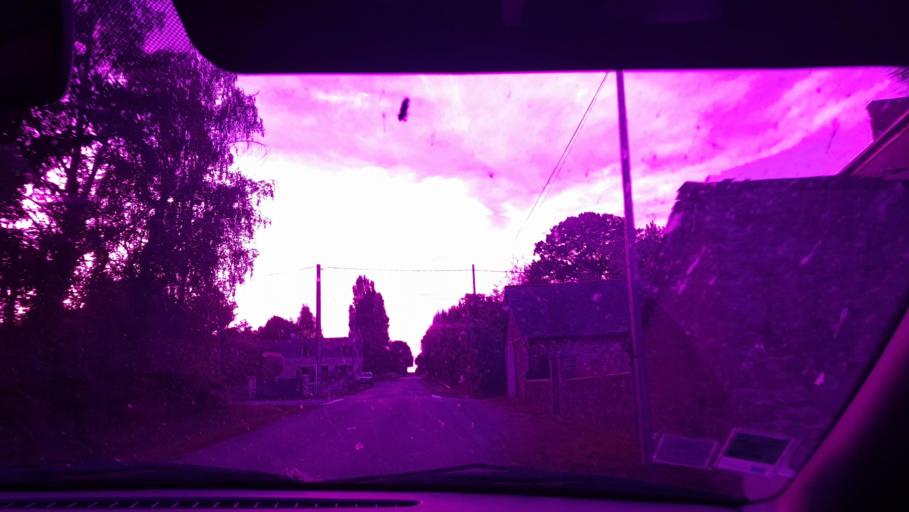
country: FR
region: Brittany
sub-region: Departement d'Ille-et-Vilaine
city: Le Pertre
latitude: 48.0430
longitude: -1.0469
